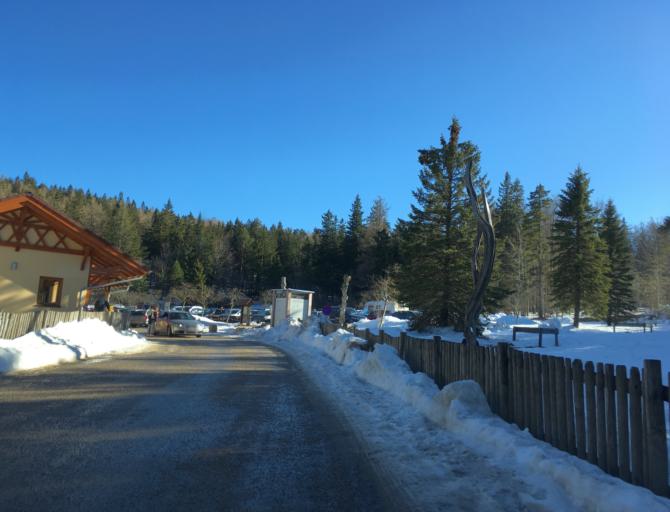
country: AT
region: Lower Austria
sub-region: Politischer Bezirk Wiener Neustadt
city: Miesenbach
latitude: 47.8348
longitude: 16.0160
